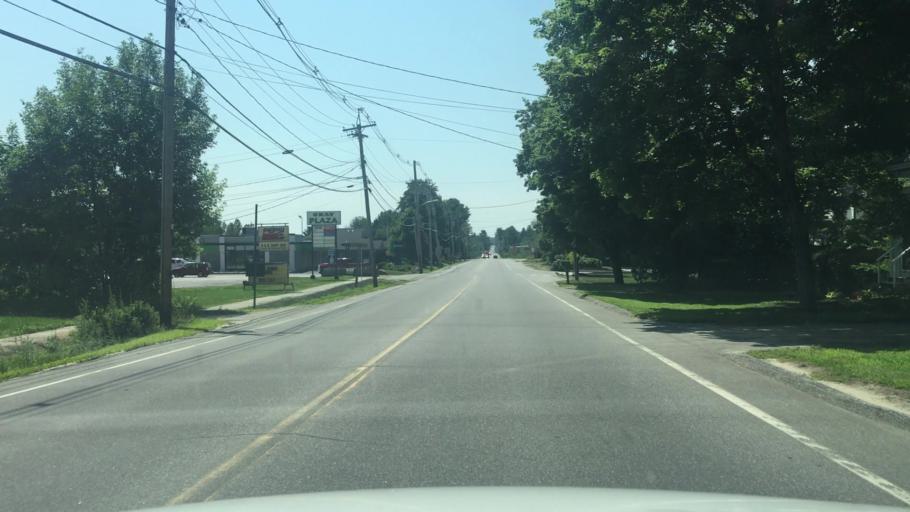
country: US
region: Maine
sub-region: Cumberland County
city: New Gloucester
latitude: 43.8826
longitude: -70.3299
